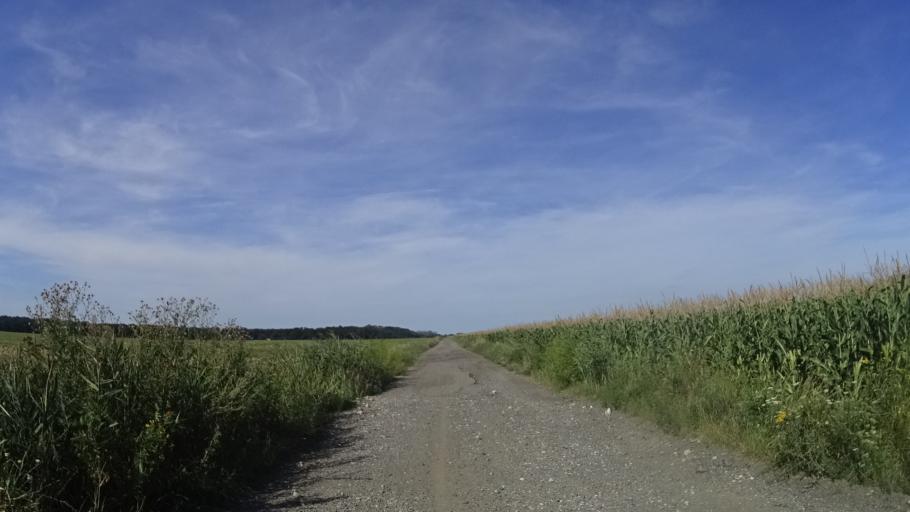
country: AT
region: Lower Austria
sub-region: Politischer Bezirk Ganserndorf
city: Durnkrut
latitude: 48.4491
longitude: 16.8837
